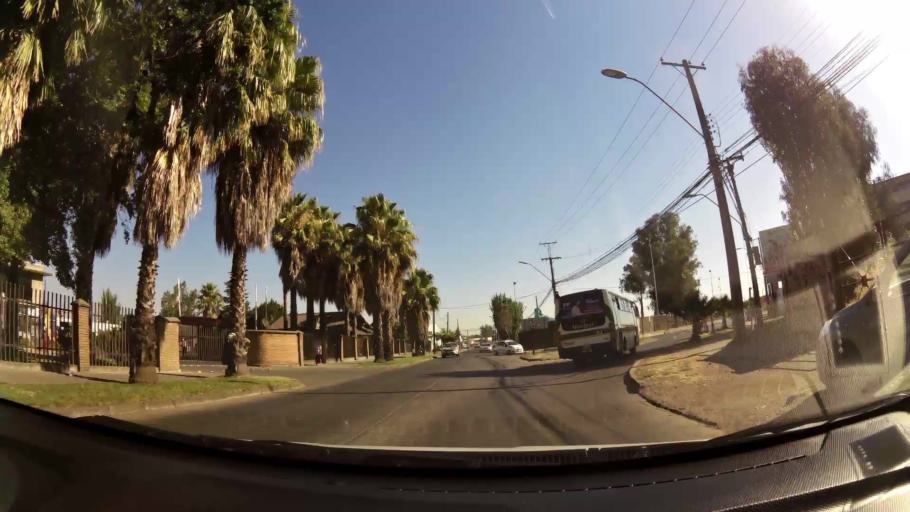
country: CL
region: Maule
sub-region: Provincia de Curico
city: Curico
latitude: -34.9857
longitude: -71.2490
